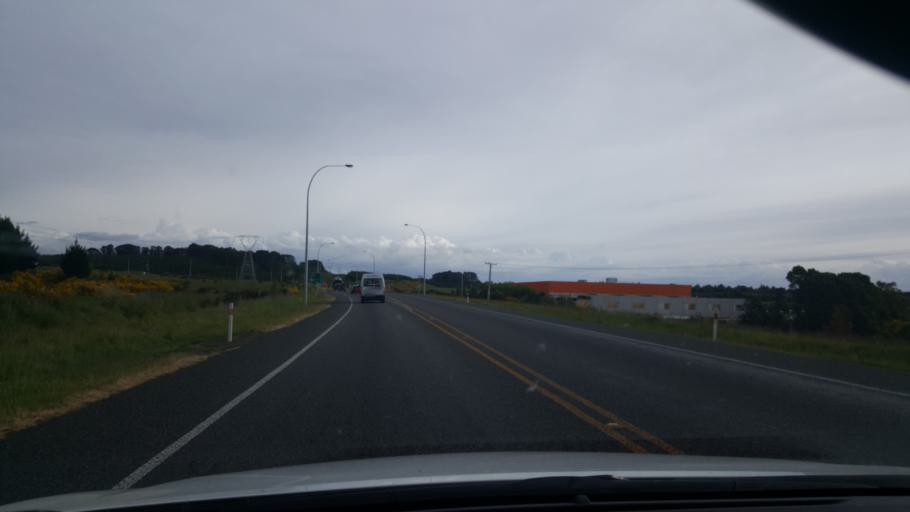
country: NZ
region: Waikato
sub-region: Taupo District
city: Taupo
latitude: -38.7007
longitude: 176.1119
